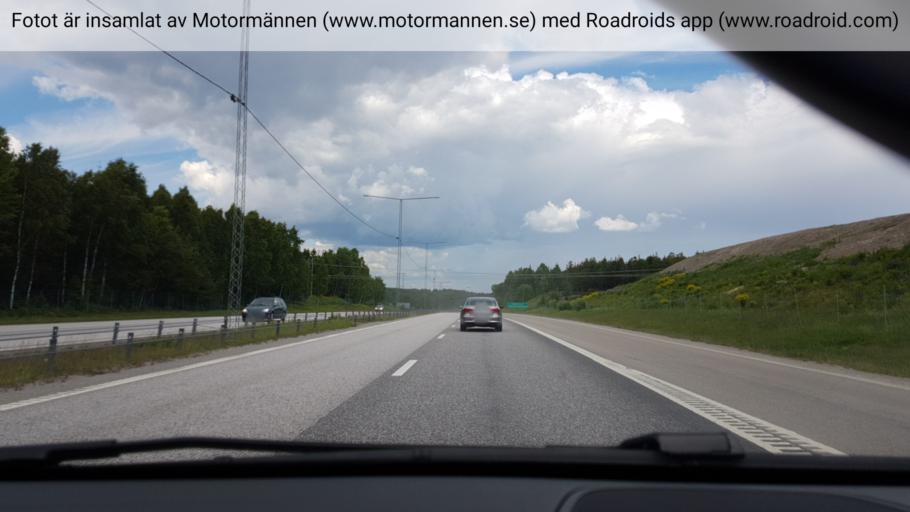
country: SE
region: Stockholm
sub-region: Haninge Kommun
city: Jordbro
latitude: 59.1107
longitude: 18.1264
